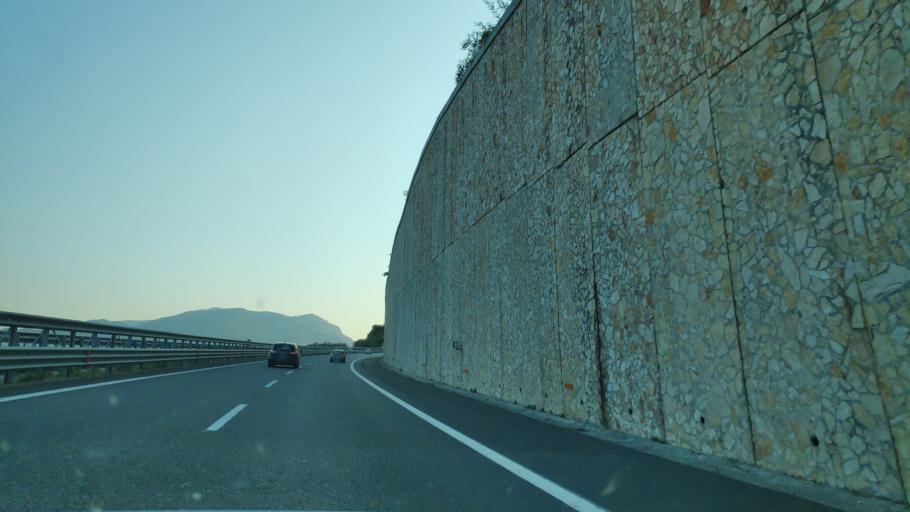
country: IT
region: Calabria
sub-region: Provincia di Catanzaro
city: Nocera Scalo
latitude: 39.0380
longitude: 16.1374
